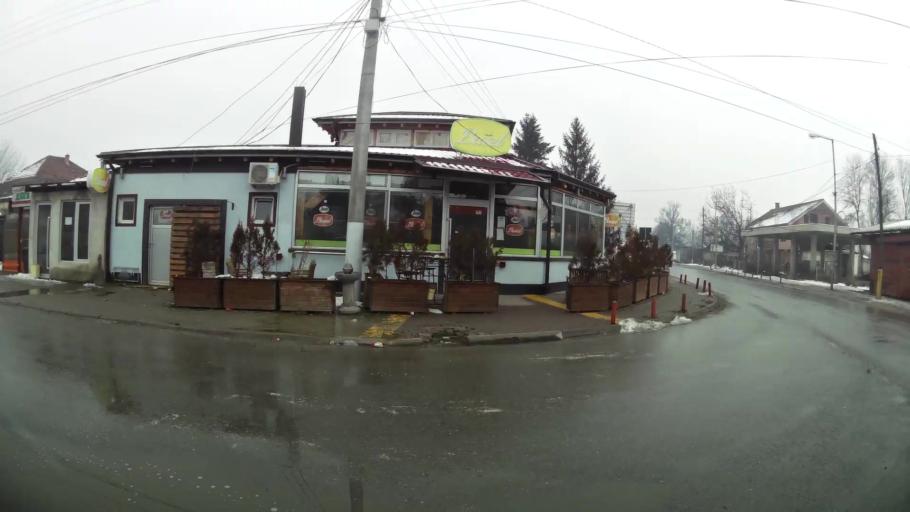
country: MK
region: Petrovec
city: Petrovec
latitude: 41.9375
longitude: 21.6180
